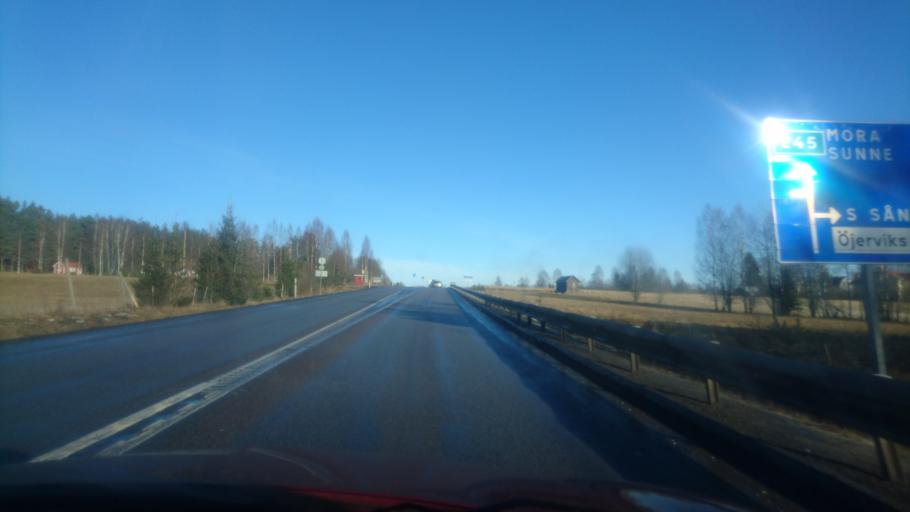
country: SE
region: Vaermland
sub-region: Sunne Kommun
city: Sunne
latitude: 59.7749
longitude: 13.0963
